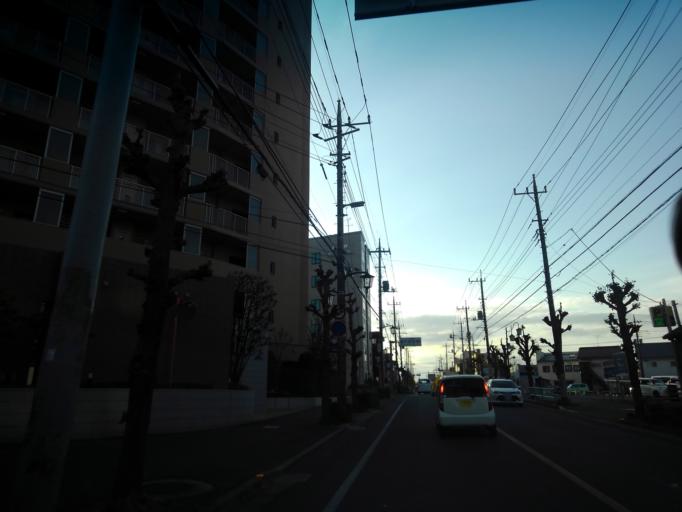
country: JP
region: Saitama
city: Tokorozawa
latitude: 35.7898
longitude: 139.4602
